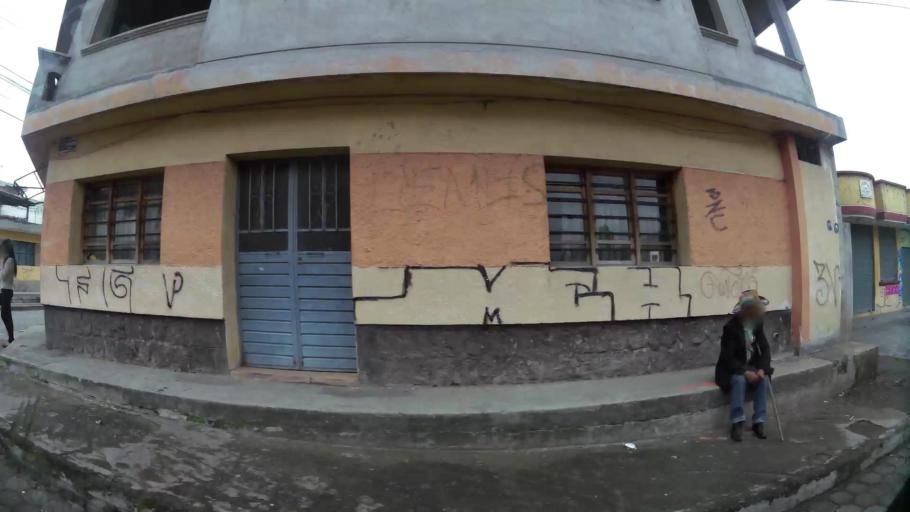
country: EC
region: Pichincha
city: Sangolqui
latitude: -0.3307
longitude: -78.4736
